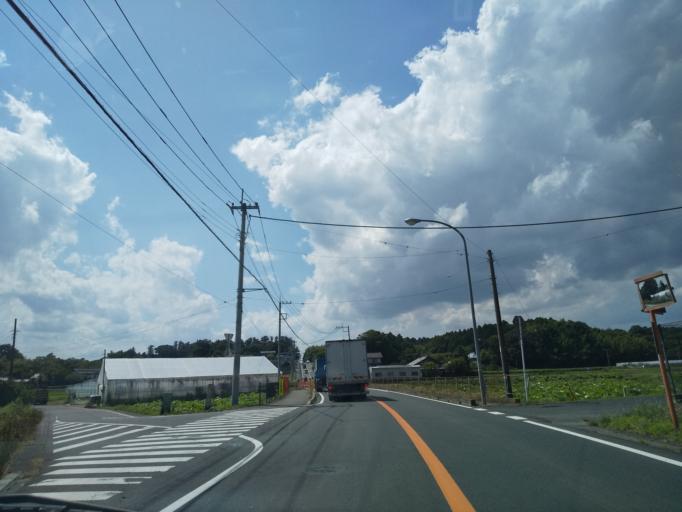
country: JP
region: Ibaraki
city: Ishioka
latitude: 36.1630
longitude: 140.3712
